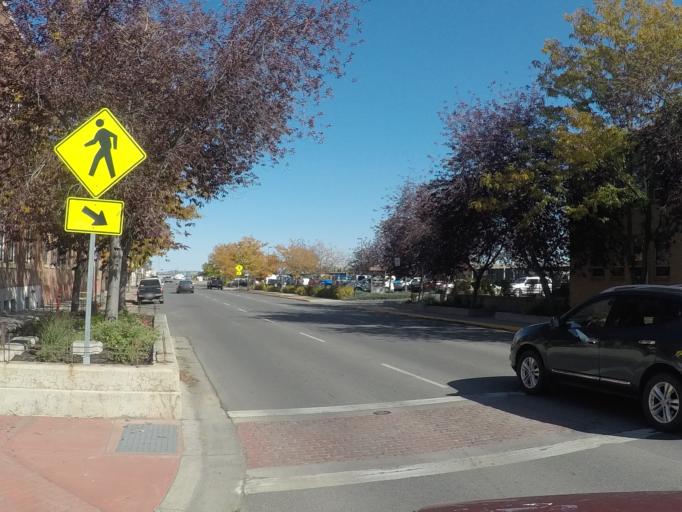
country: US
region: Montana
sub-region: Yellowstone County
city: Billings
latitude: 45.7843
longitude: -108.4988
